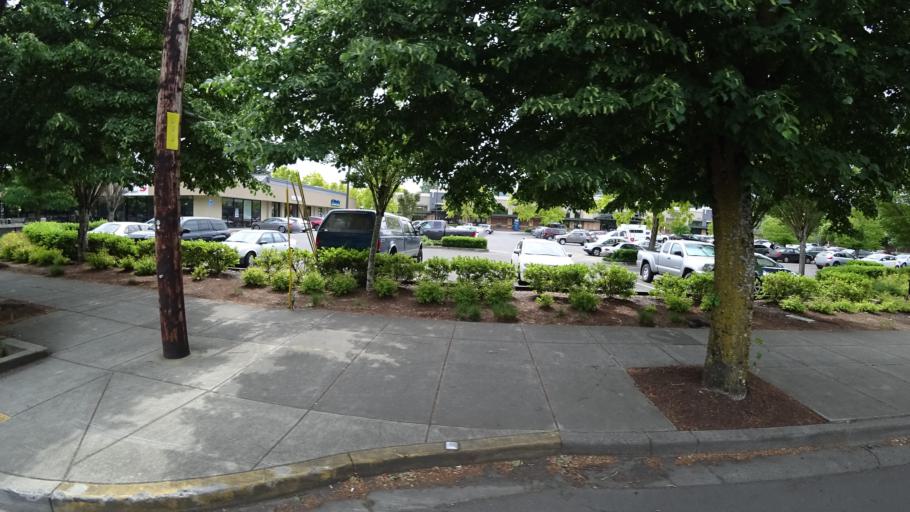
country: US
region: Oregon
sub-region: Washington County
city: West Haven
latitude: 45.5886
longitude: -122.7524
